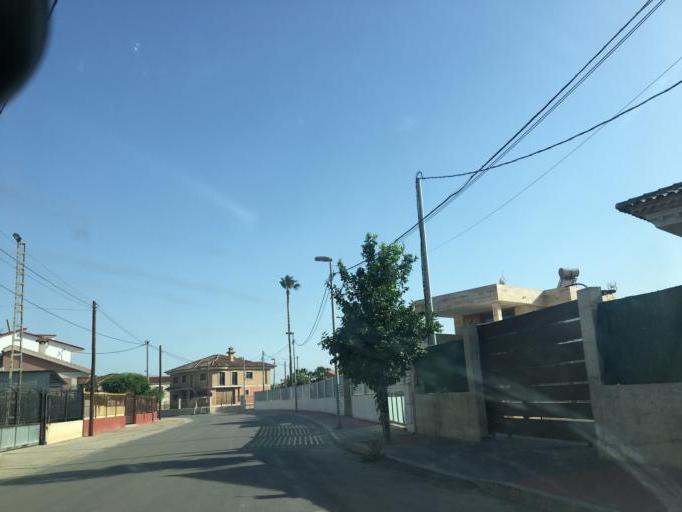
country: ES
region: Murcia
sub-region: Murcia
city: Santomera
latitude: 38.0321
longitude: -1.0690
